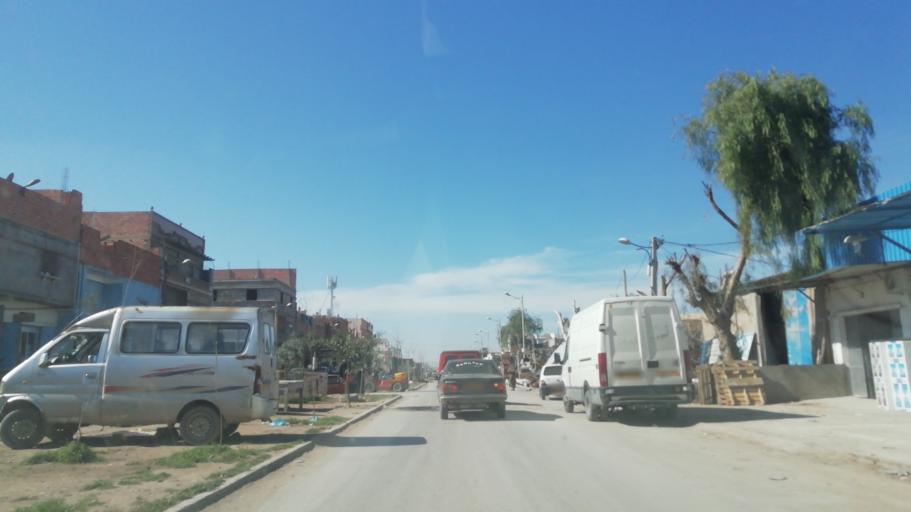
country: DZ
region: Oran
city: Es Senia
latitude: 35.6455
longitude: -0.5817
